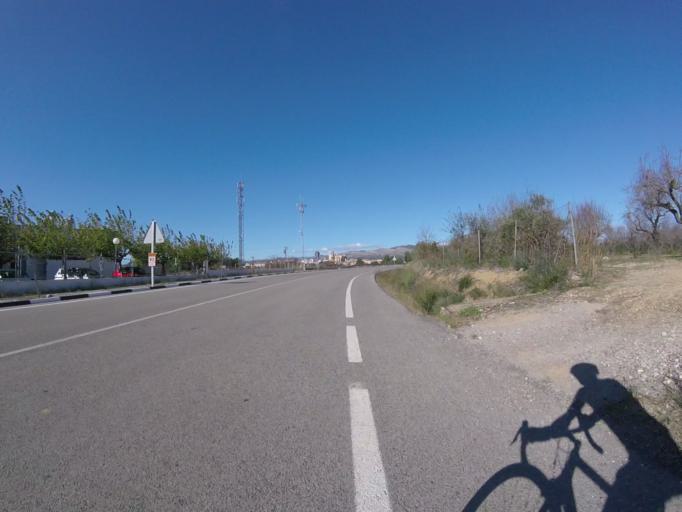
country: ES
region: Valencia
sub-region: Provincia de Castello
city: Chert/Xert
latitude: 40.4653
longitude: 0.1886
